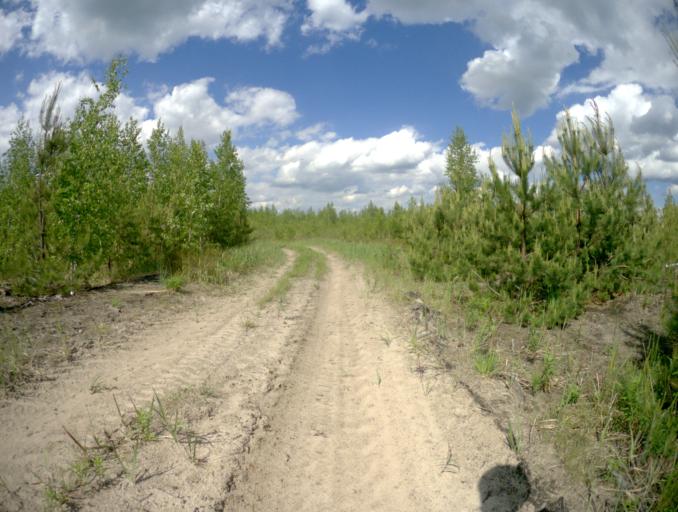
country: RU
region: Vladimir
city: Velikodvorskiy
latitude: 55.2883
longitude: 40.8915
